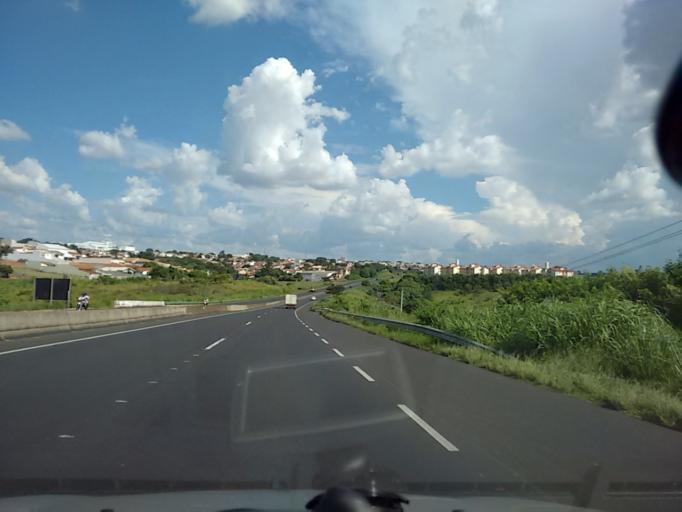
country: BR
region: Sao Paulo
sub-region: Marilia
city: Marilia
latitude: -22.1889
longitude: -49.9682
